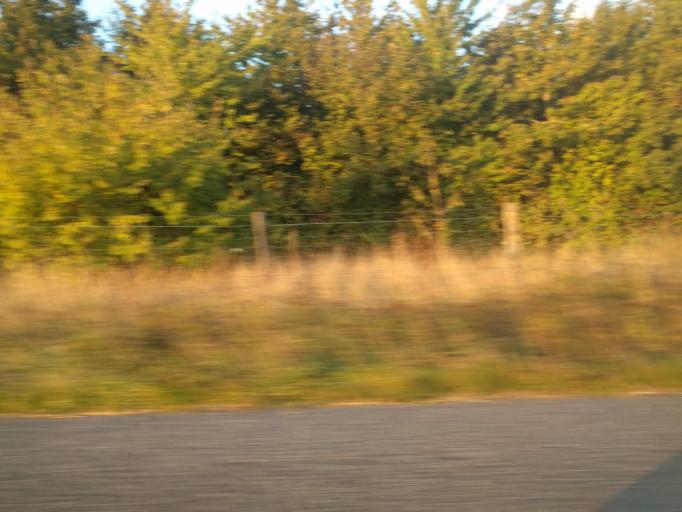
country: DK
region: South Denmark
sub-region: Nyborg Kommune
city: Ullerslev
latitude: 55.3381
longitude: 10.7175
